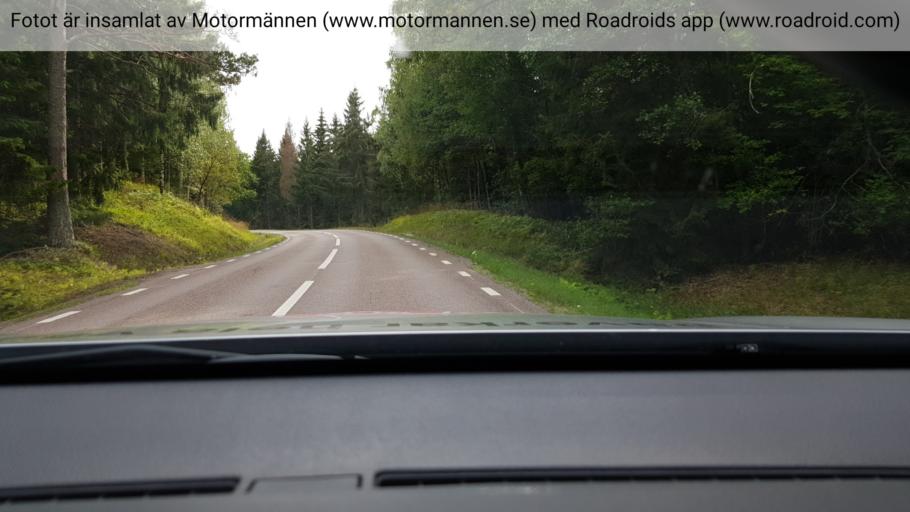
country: SE
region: Soedermanland
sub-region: Gnesta Kommun
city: Gnesta
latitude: 58.9852
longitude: 17.1546
